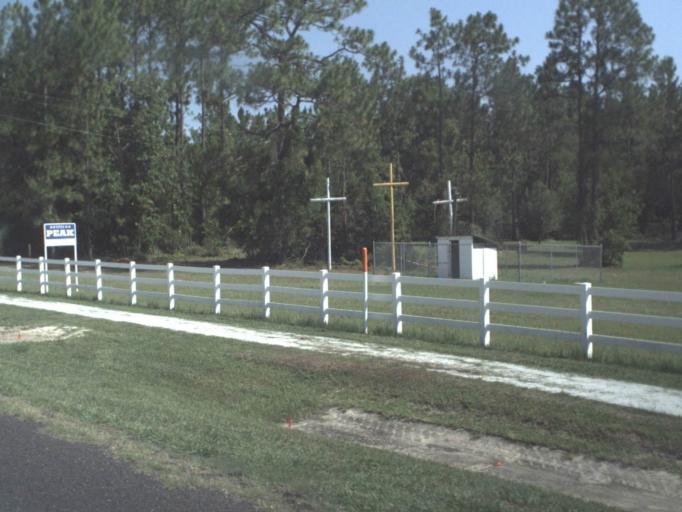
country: US
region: Georgia
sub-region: Charlton County
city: Folkston
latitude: 30.7692
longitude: -81.9729
